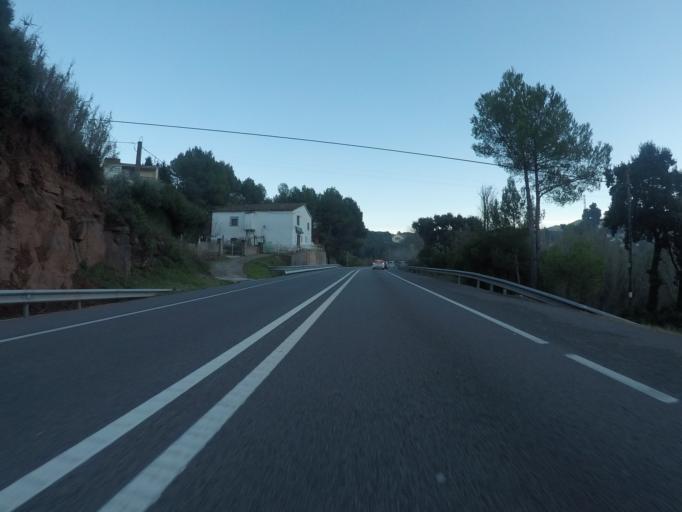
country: ES
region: Catalonia
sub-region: Provincia de Barcelona
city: Monistrol de Montserrat
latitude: 41.6141
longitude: 1.8719
